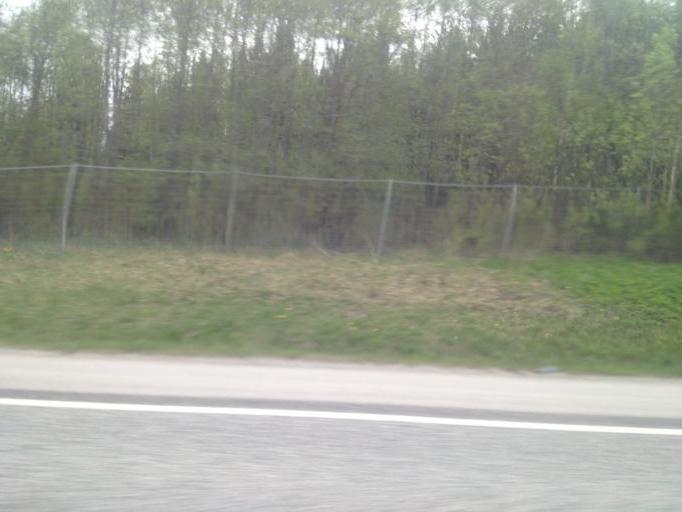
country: FI
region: Uusimaa
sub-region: Helsinki
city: Nurmijaervi
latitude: 60.4225
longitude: 24.8255
